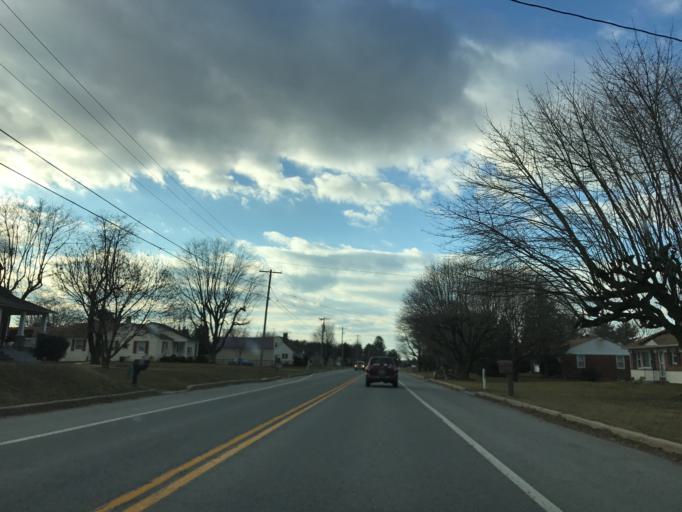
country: US
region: Maryland
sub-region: Cecil County
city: Rising Sun
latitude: 39.6902
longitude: -76.0436
